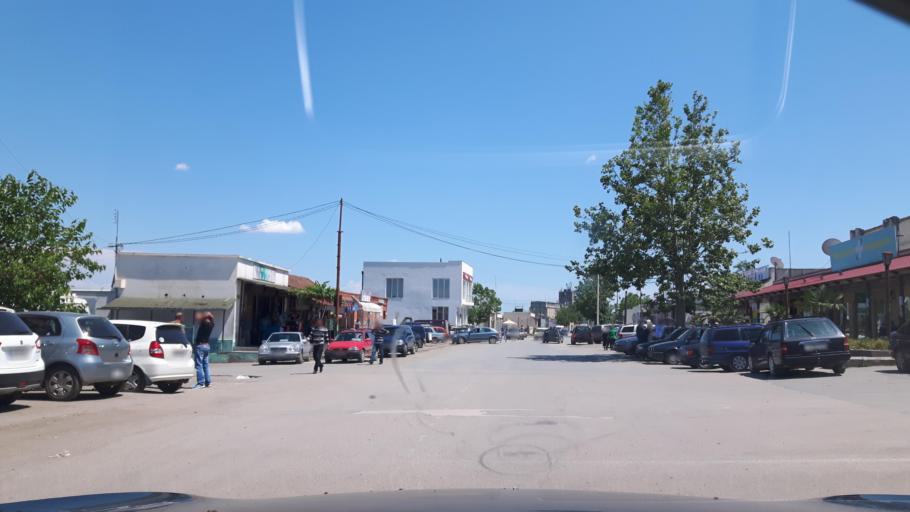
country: GE
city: Tsnori
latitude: 41.6208
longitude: 45.9795
